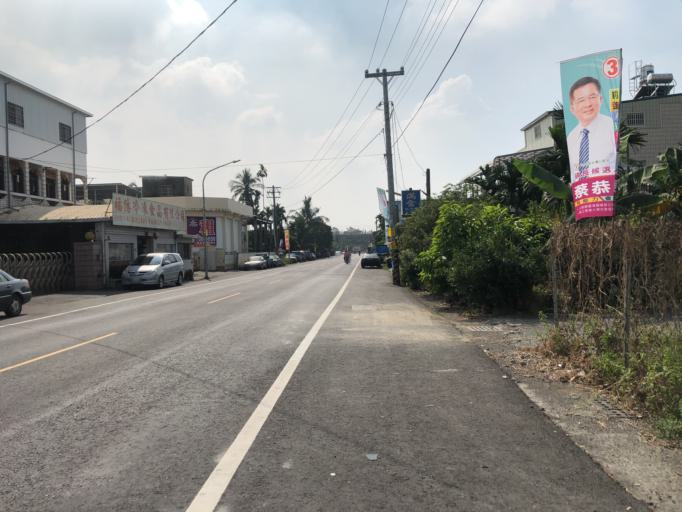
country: TW
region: Taiwan
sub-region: Pingtung
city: Pingtung
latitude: 22.5496
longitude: 120.5340
